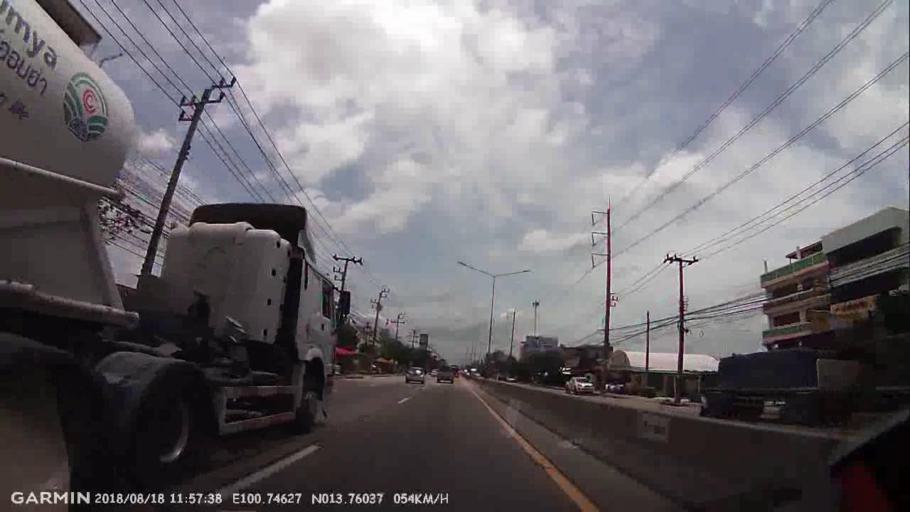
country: TH
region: Bangkok
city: Lat Krabang
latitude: 13.7605
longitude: 100.7463
